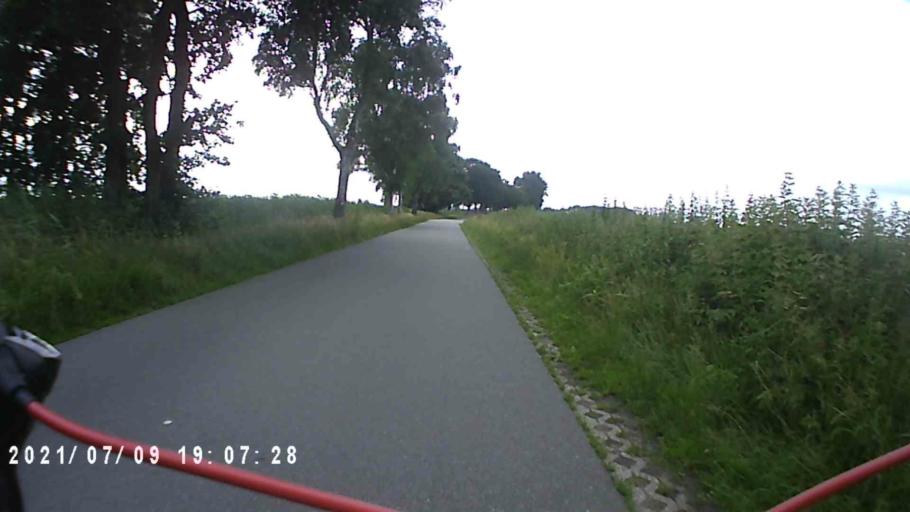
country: NL
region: Groningen
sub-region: Gemeente Veendam
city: Veendam
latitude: 53.0601
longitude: 6.8755
